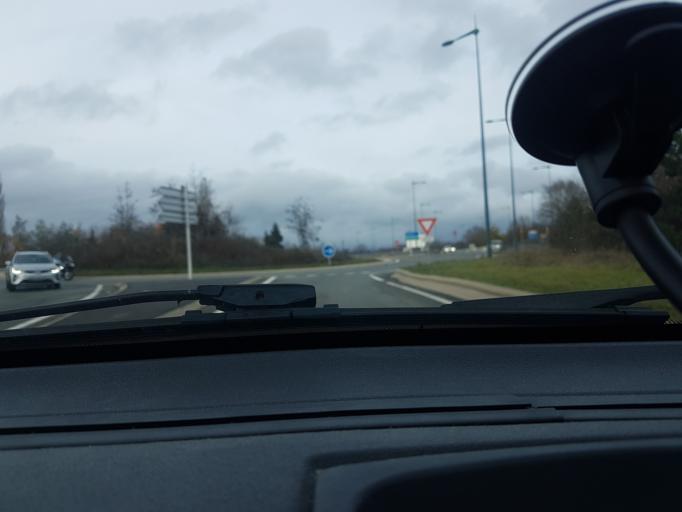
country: FR
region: Franche-Comte
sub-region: Territoire de Belfort
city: Danjoutin
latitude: 47.6175
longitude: 6.8597
